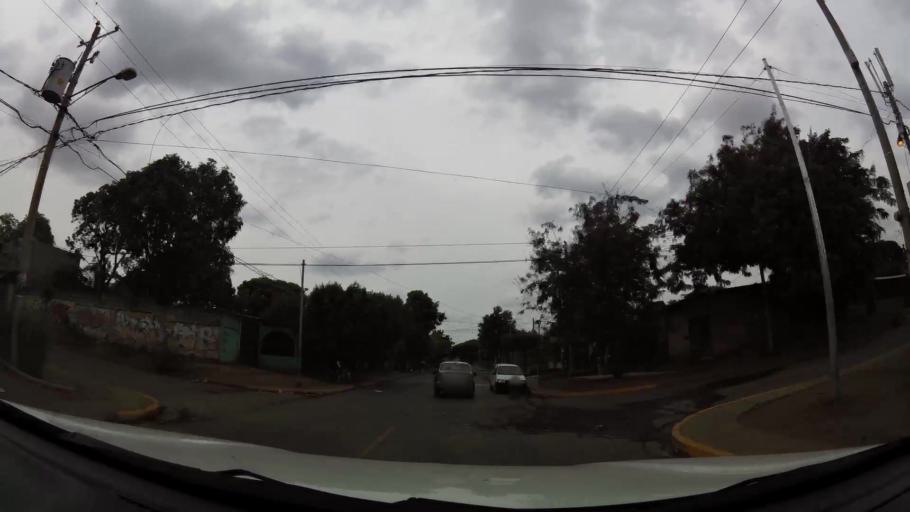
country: NI
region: Managua
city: Managua
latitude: 12.1184
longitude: -86.1959
